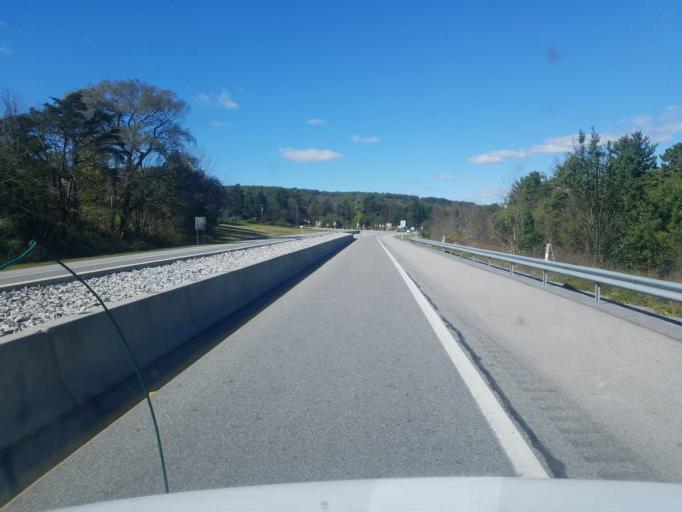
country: US
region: Pennsylvania
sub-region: Bedford County
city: Bedford
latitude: 40.0356
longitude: -78.5202
